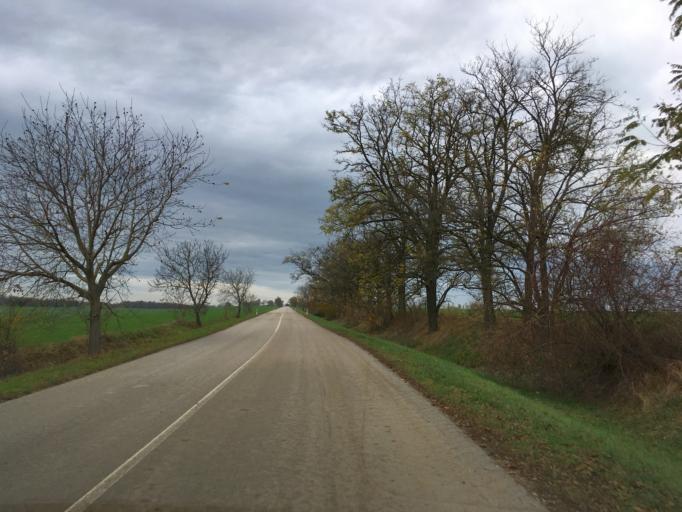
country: SK
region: Nitriansky
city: Svodin
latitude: 48.0235
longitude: 18.4058
